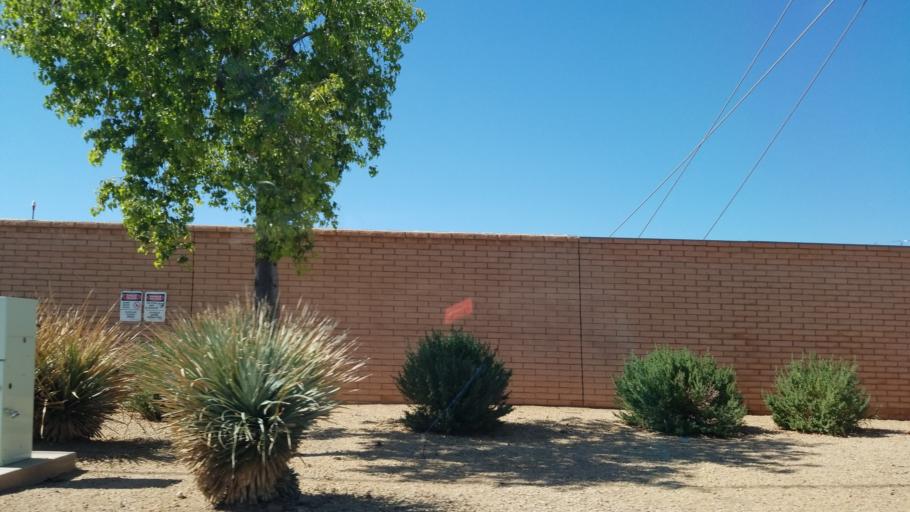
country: US
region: Arizona
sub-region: Maricopa County
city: Tolleson
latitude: 33.4900
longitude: -112.2553
